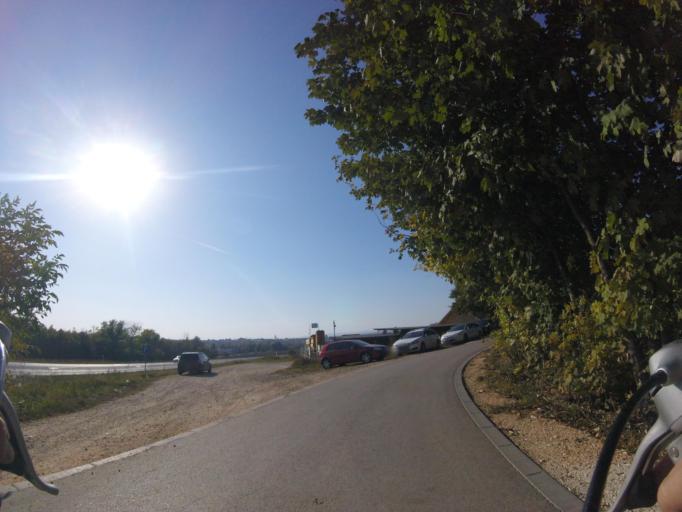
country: HU
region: Fejer
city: Bicske
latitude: 47.4940
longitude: 18.6550
